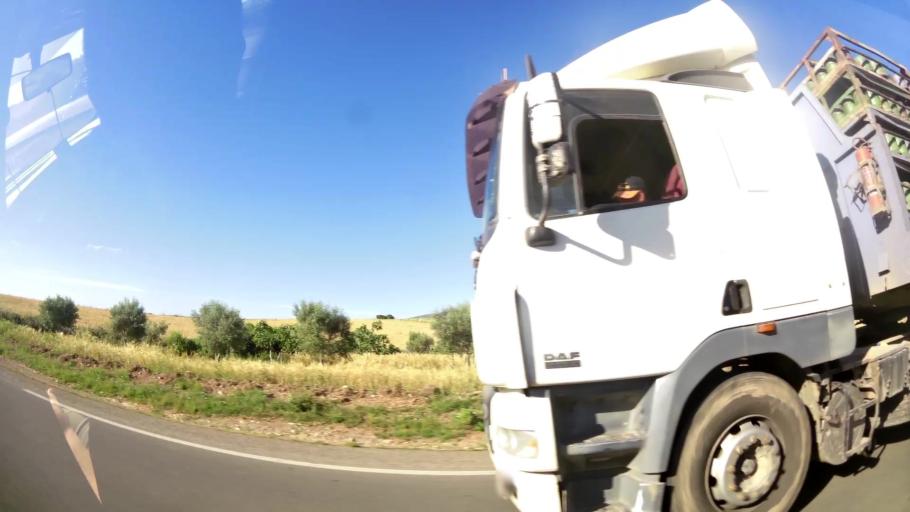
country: MA
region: Oriental
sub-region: Berkane-Taourirt
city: Ahfir
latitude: 34.9760
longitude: -2.1304
